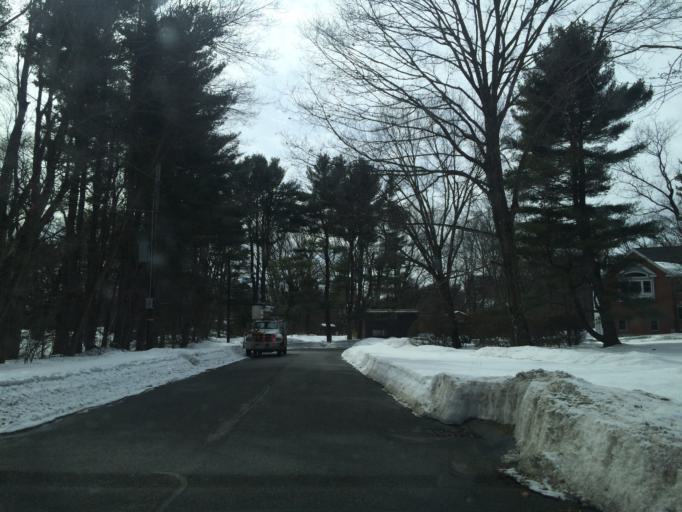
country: US
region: Massachusetts
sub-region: Middlesex County
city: Lexington
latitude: 42.4511
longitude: -71.1981
